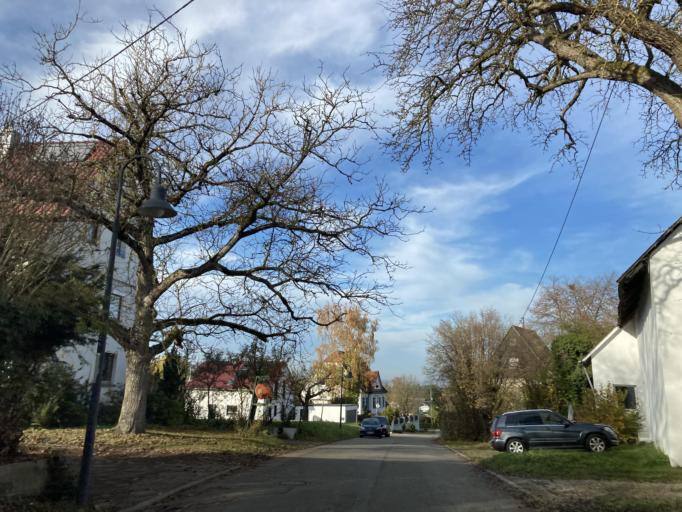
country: DE
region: Baden-Wuerttemberg
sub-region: Regierungsbezirk Stuttgart
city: Bondorf
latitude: 48.4721
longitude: 8.8160
